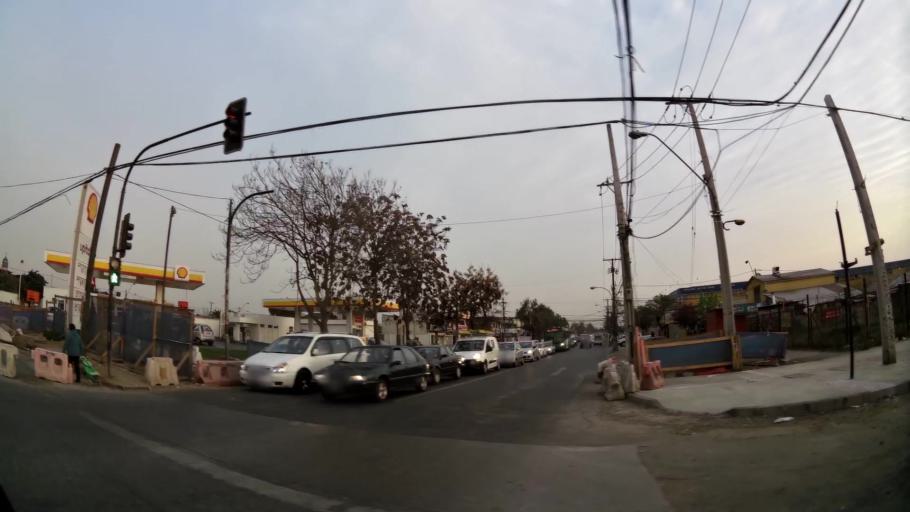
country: CL
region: Santiago Metropolitan
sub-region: Provincia de Santiago
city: Lo Prado
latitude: -33.5095
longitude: -70.7756
